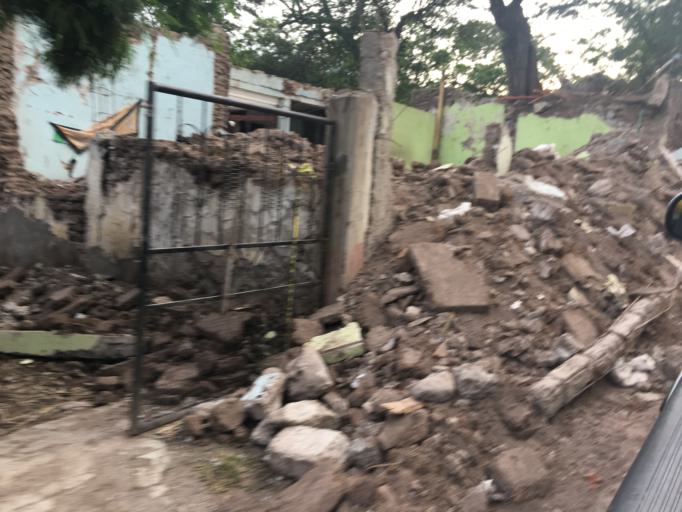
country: MX
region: Morelos
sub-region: Axochiapan
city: Quebrantadero
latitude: 18.5178
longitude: -98.8117
